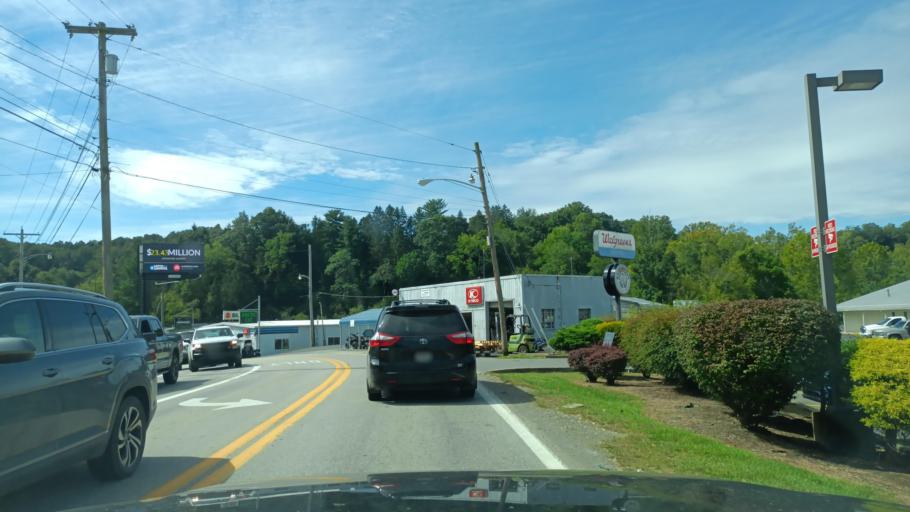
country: US
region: West Virginia
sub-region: Harrison County
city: Bridgeport
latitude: 39.2832
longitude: -80.2563
